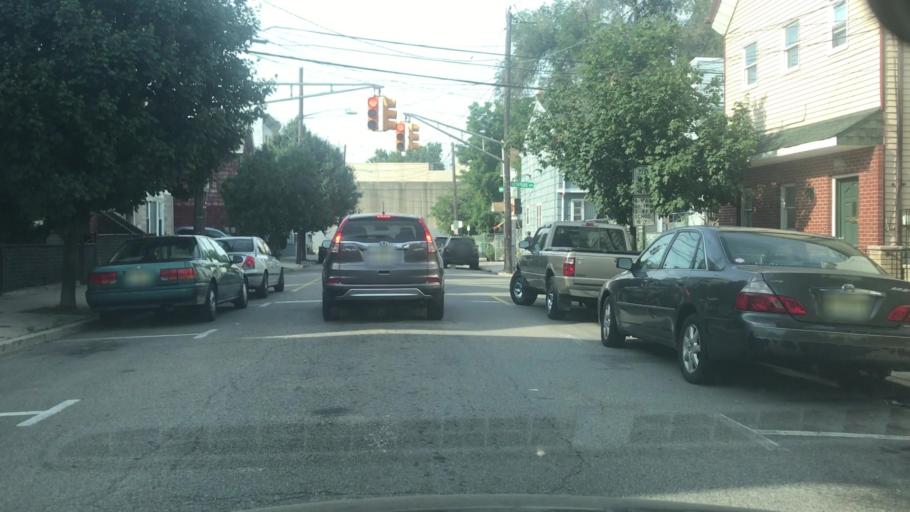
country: US
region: New Jersey
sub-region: Hudson County
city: East Newark
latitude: 40.7484
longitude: -74.1621
